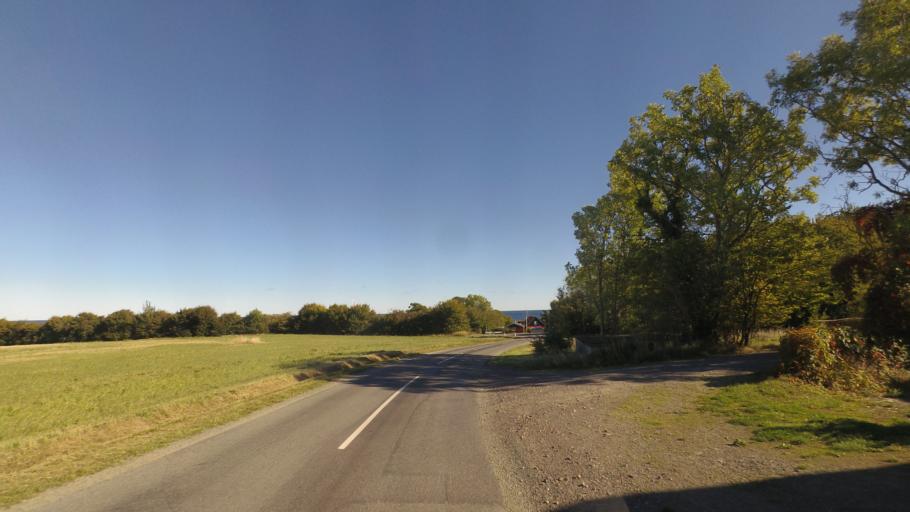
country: DK
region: Capital Region
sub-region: Bornholm Kommune
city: Nexo
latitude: 55.1102
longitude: 15.1386
